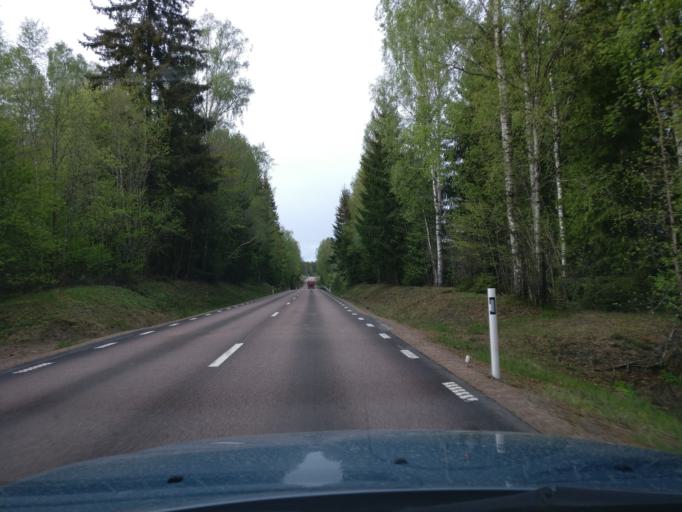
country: SE
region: Vaermland
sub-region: Forshaga Kommun
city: Deje
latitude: 59.6494
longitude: 13.4418
